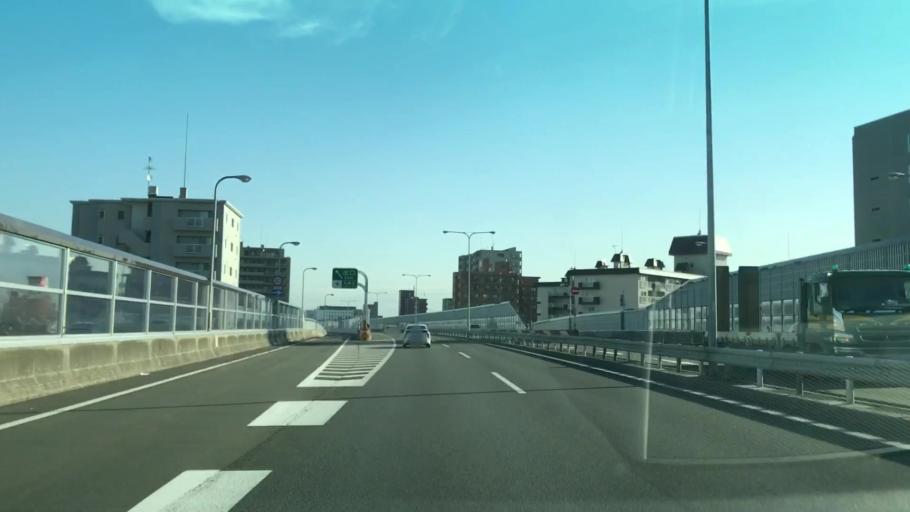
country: JP
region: Hokkaido
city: Sapporo
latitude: 43.1002
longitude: 141.3341
